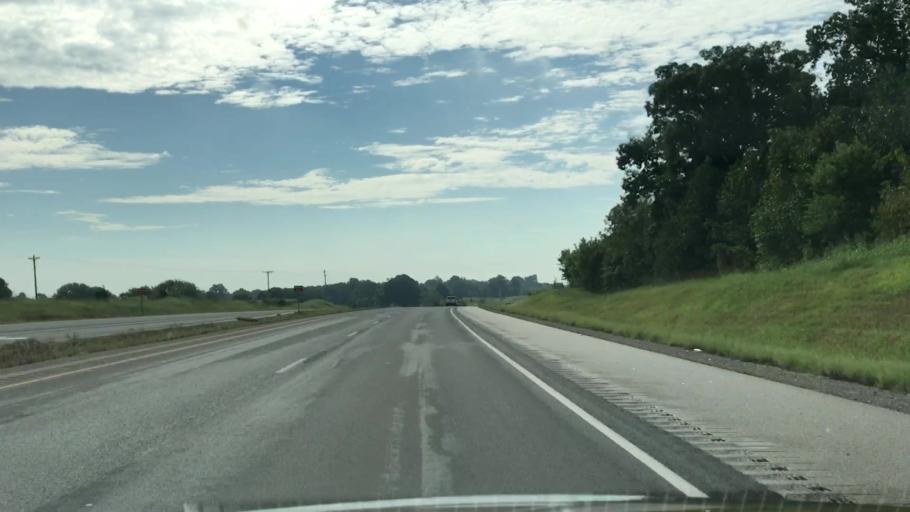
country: US
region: Kentucky
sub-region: Warren County
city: Plano
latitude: 36.8593
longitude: -86.3433
